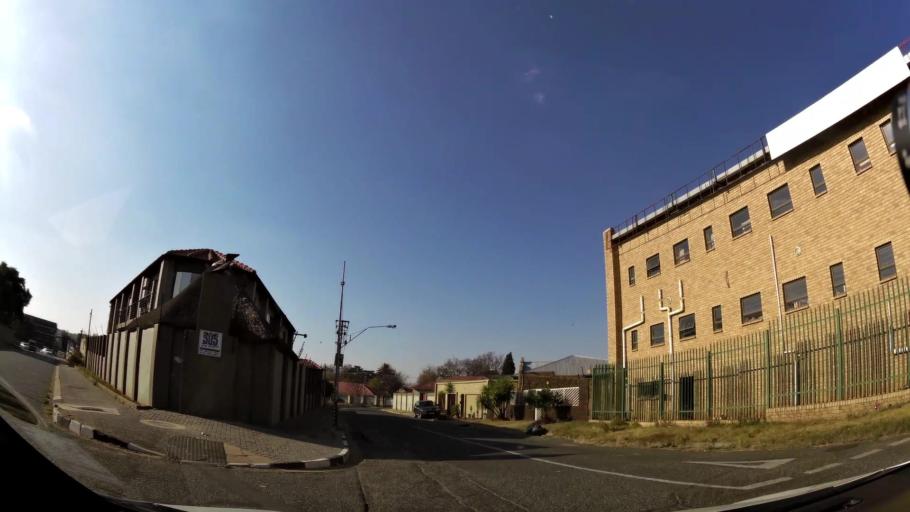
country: ZA
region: Gauteng
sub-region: City of Johannesburg Metropolitan Municipality
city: Johannesburg
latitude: -26.2354
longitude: 28.0211
